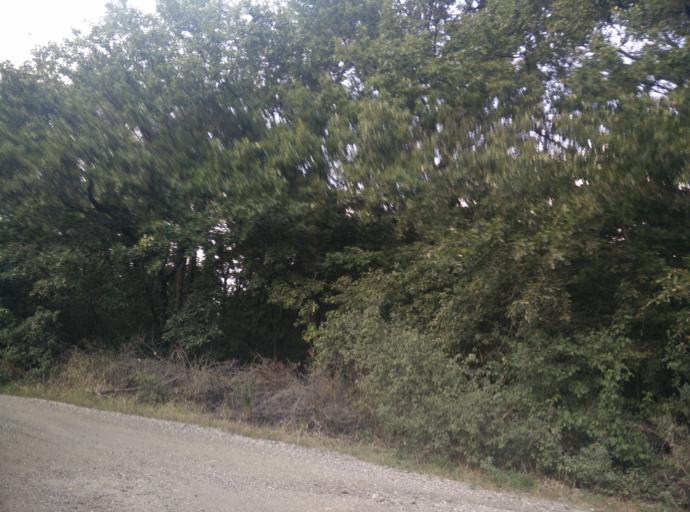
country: HU
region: Pest
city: Paty
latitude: 47.5022
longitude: 18.8518
